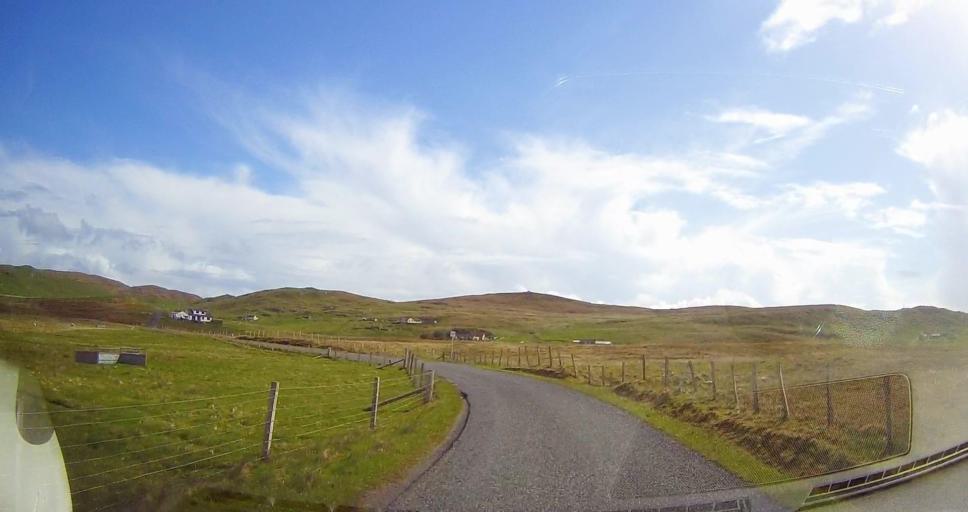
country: GB
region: Scotland
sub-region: Shetland Islands
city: Lerwick
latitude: 60.5902
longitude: -1.3340
